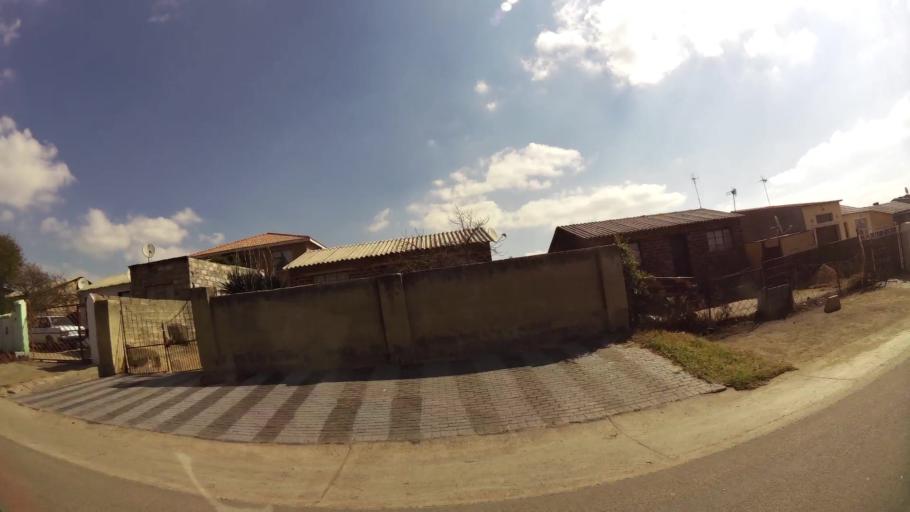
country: ZA
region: Gauteng
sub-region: Ekurhuleni Metropolitan Municipality
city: Tembisa
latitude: -26.0150
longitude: 28.2006
